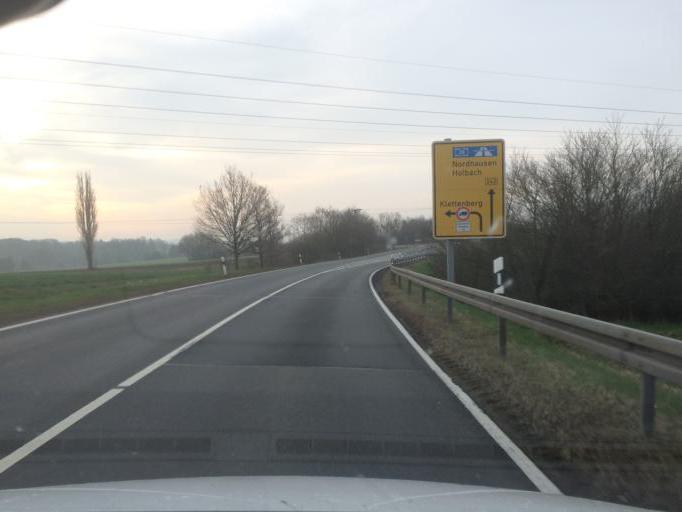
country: DE
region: Lower Saxony
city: Walkenried
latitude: 51.5443
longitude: 10.5907
